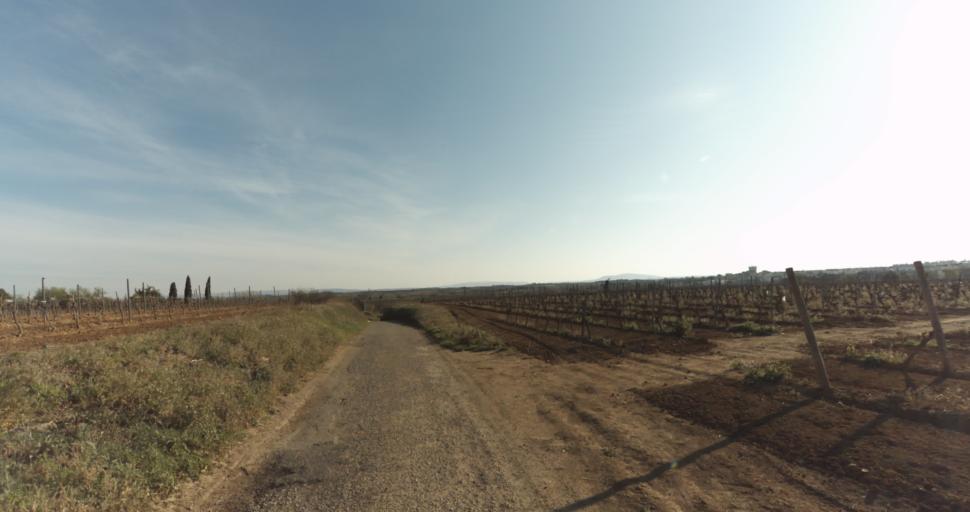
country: FR
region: Languedoc-Roussillon
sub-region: Departement de l'Herault
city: Marseillan
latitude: 43.3628
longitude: 3.5107
